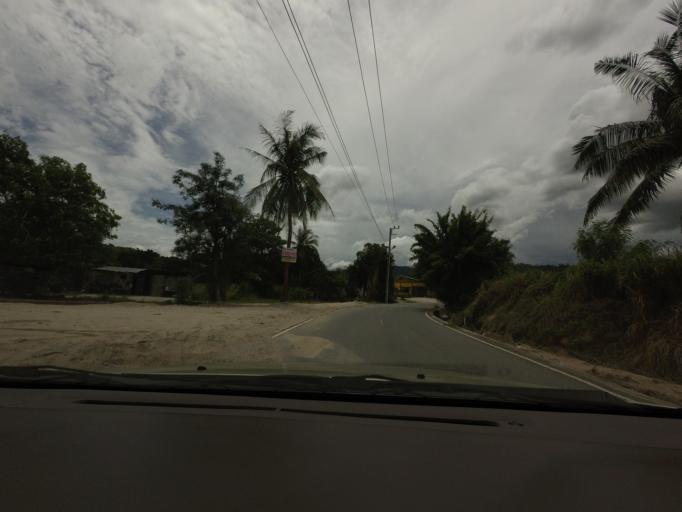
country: TH
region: Chon Buri
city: Si Racha
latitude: 13.2162
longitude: 101.0412
